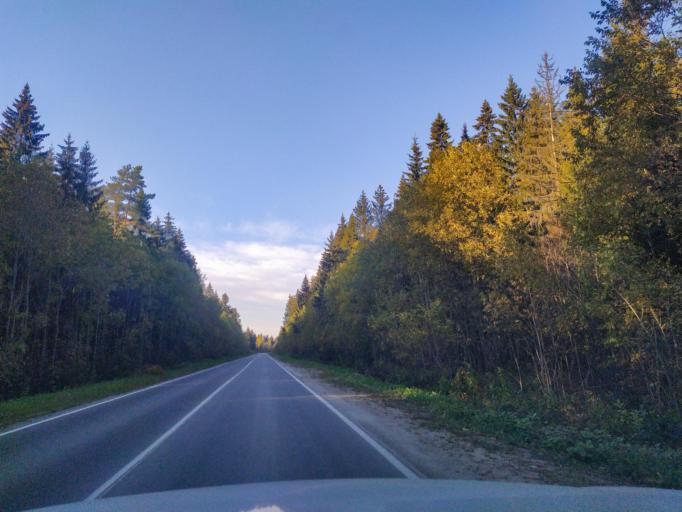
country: RU
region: Leningrad
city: Siverskiy
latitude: 59.3041
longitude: 30.0341
